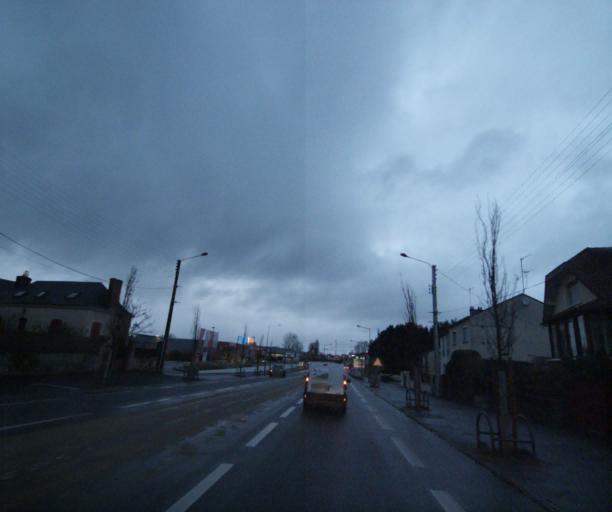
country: FR
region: Pays de la Loire
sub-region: Departement de la Sarthe
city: Coulaines
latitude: 48.0237
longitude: 0.1825
